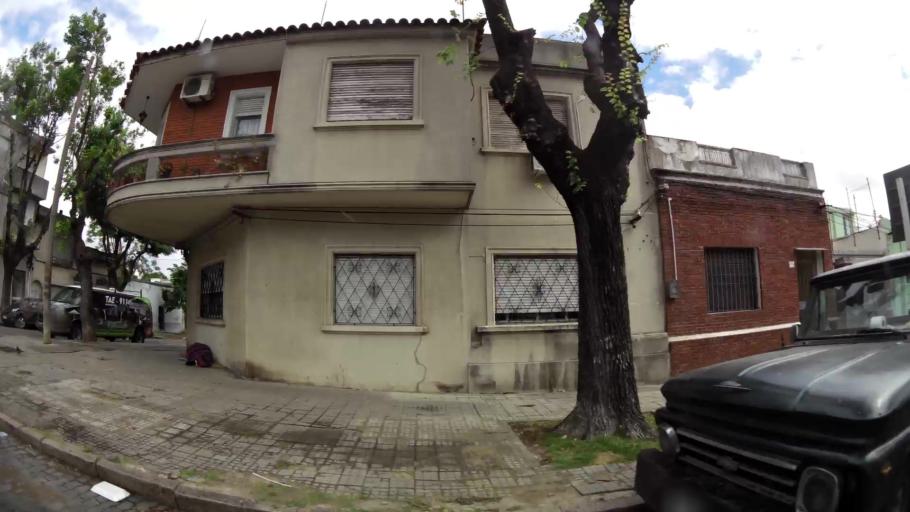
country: UY
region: Montevideo
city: Montevideo
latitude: -34.8710
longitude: -56.1690
